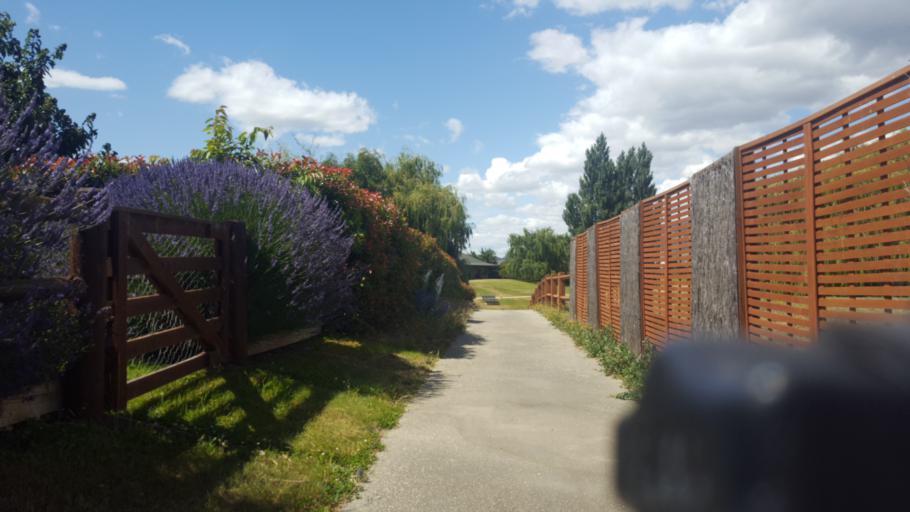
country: NZ
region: Otago
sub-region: Queenstown-Lakes District
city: Wanaka
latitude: -44.9759
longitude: 169.2427
